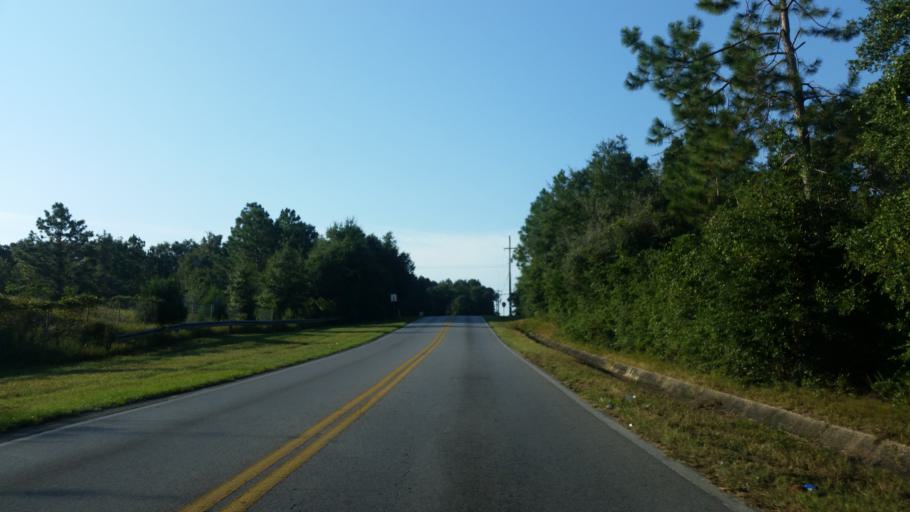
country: US
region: Florida
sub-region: Santa Rosa County
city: Bagdad
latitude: 30.6035
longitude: -87.0647
